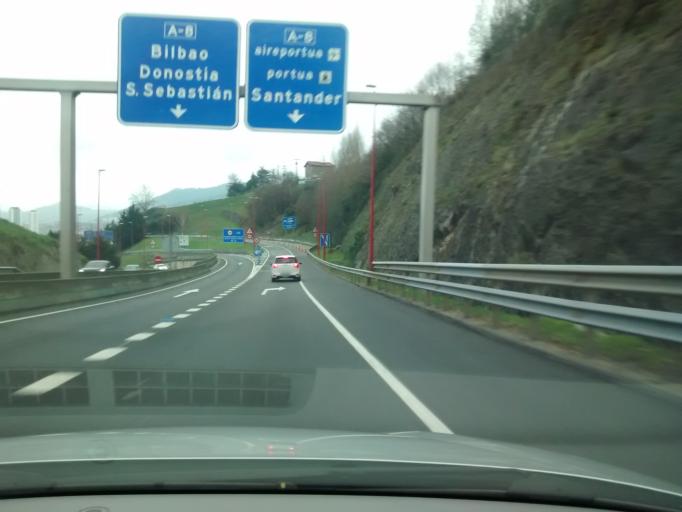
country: ES
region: Basque Country
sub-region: Bizkaia
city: Alonsotegi
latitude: 43.2693
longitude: -2.9671
